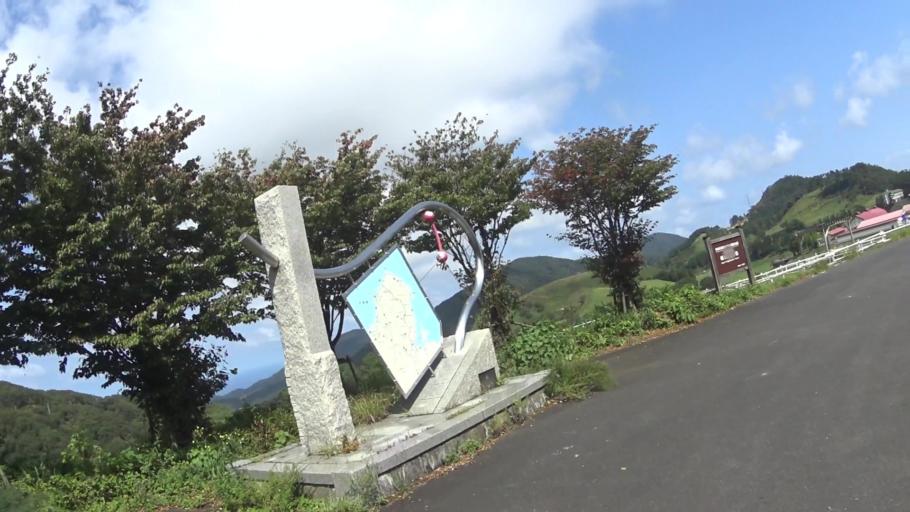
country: JP
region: Kyoto
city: Miyazu
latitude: 35.7191
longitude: 135.1892
